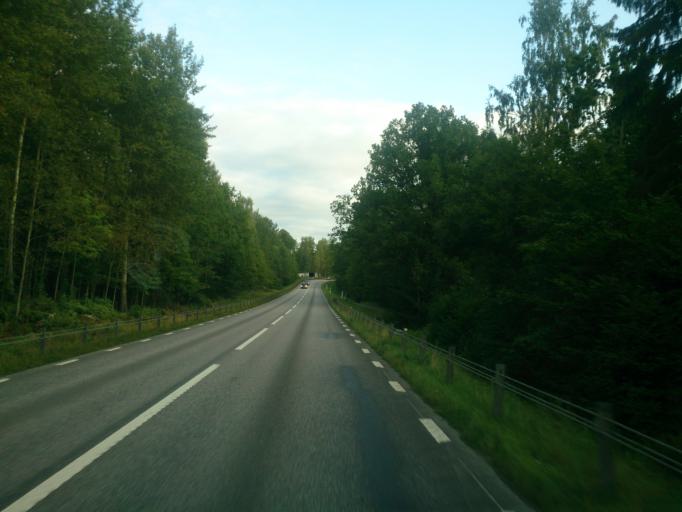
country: SE
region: OEstergoetland
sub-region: Atvidabergs Kommun
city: Atvidaberg
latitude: 58.2491
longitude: 15.9312
